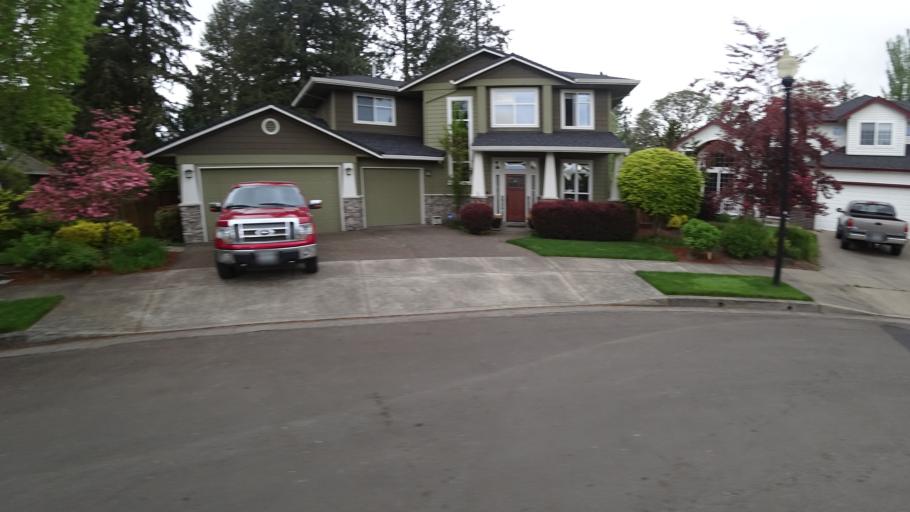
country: US
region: Oregon
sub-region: Washington County
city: Hillsboro
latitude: 45.5465
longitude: -122.9750
